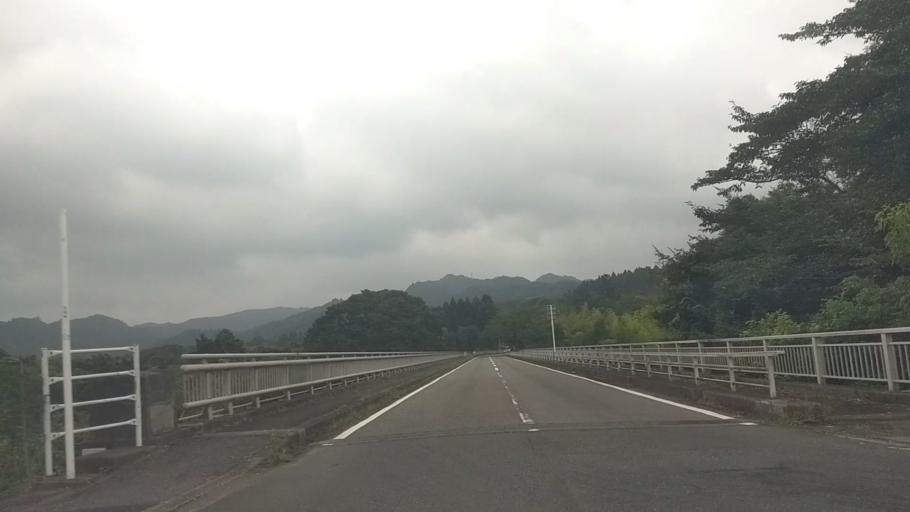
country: JP
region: Chiba
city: Kawaguchi
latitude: 35.2308
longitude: 140.0883
